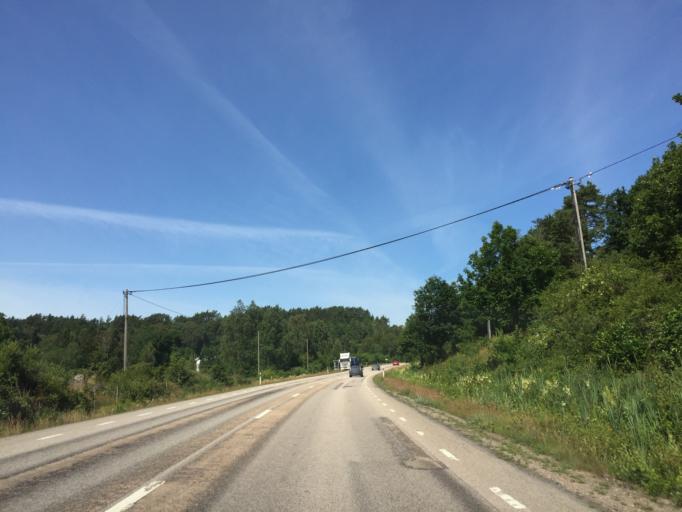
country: SE
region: Vaestra Goetaland
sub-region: Lysekils Kommun
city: Lysekil
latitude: 58.3038
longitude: 11.4933
